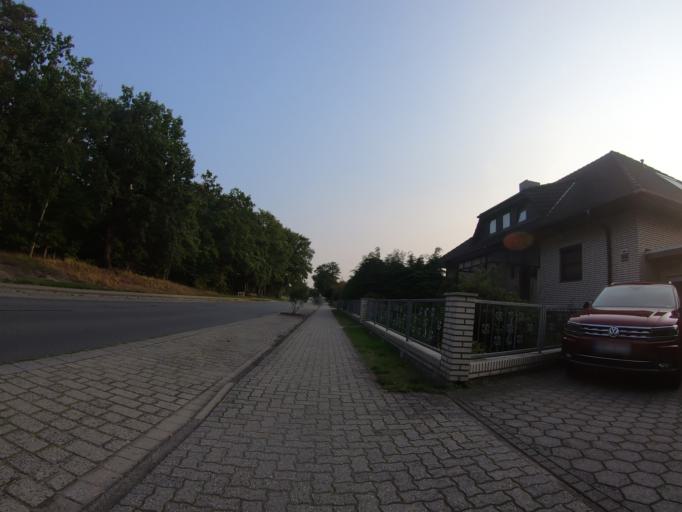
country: DE
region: Lower Saxony
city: Leiferde
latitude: 52.4464
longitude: 10.4361
